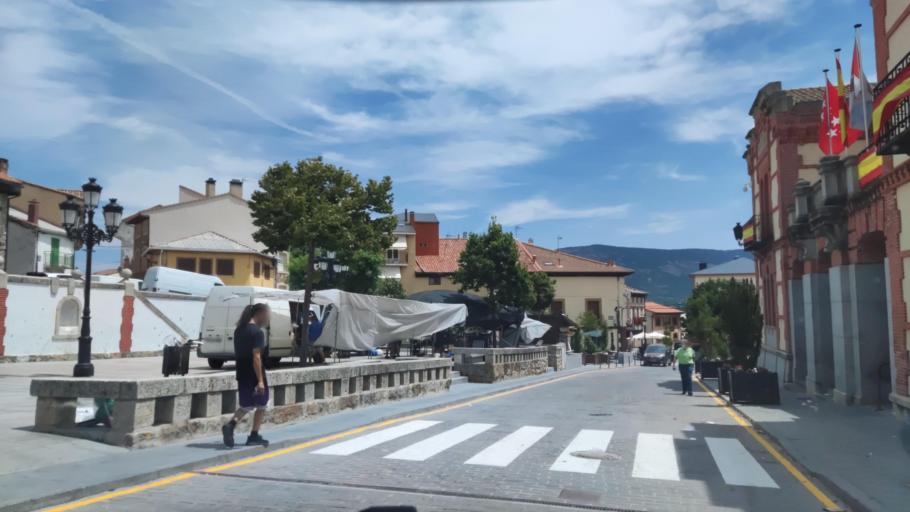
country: ES
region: Madrid
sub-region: Provincia de Madrid
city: Rascafria
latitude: 40.9043
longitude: -3.8805
